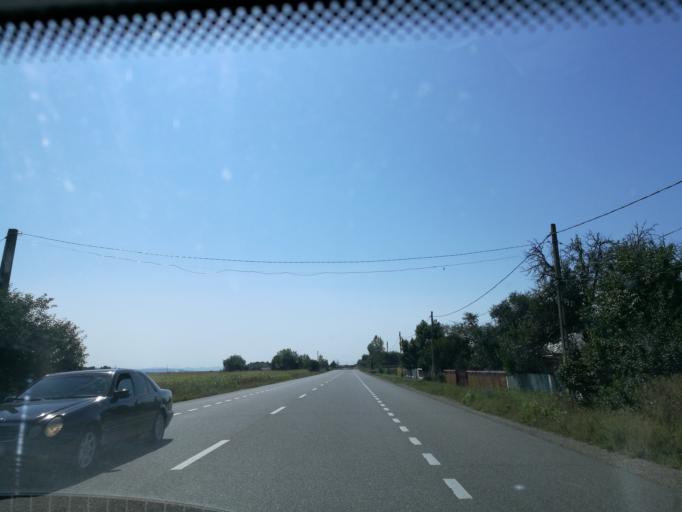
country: RO
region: Bacau
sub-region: Comuna Filipesti
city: Filipesti
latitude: 46.7896
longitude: 26.8895
